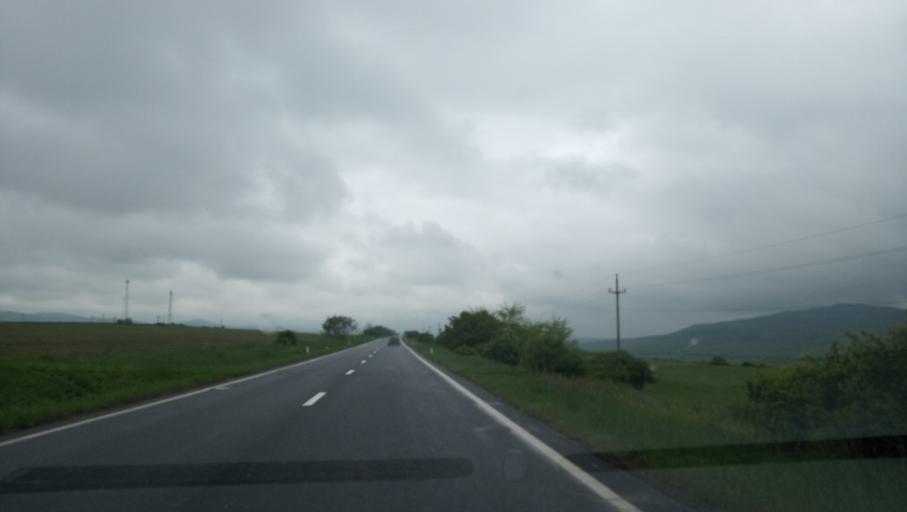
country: RO
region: Alba
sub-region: Comuna Cut
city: Cut
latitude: 45.9196
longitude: 23.6798
